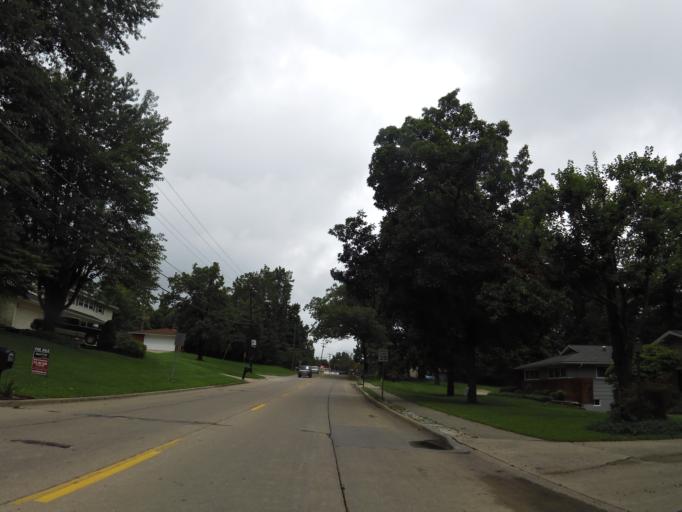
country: US
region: Missouri
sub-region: Cape Girardeau County
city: Cape Girardeau
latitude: 37.3368
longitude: -89.5520
